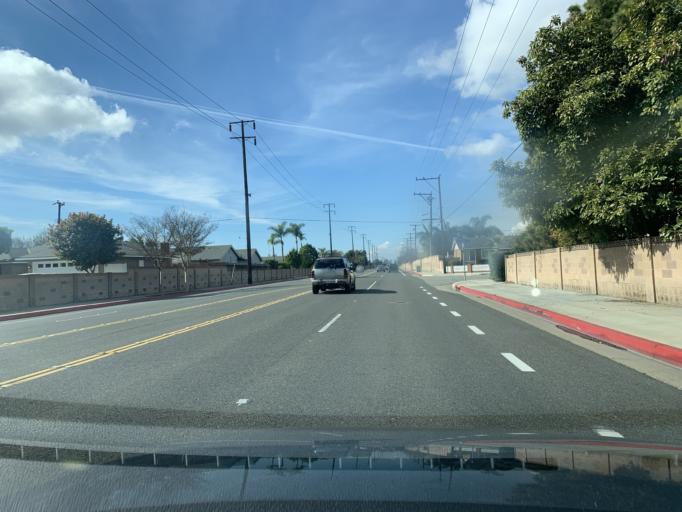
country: US
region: California
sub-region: Orange County
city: Westminster
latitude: 33.7373
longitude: -118.0189
